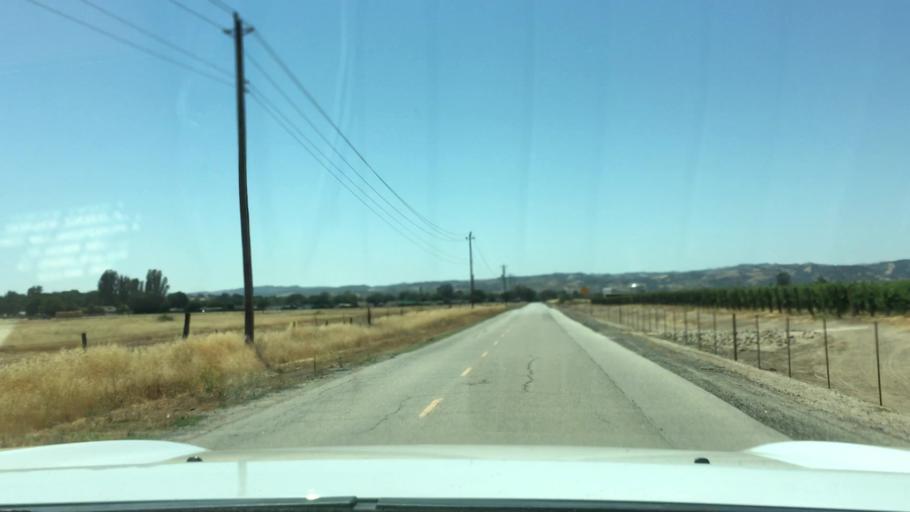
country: US
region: California
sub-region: San Luis Obispo County
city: Paso Robles
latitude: 35.6119
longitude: -120.6338
